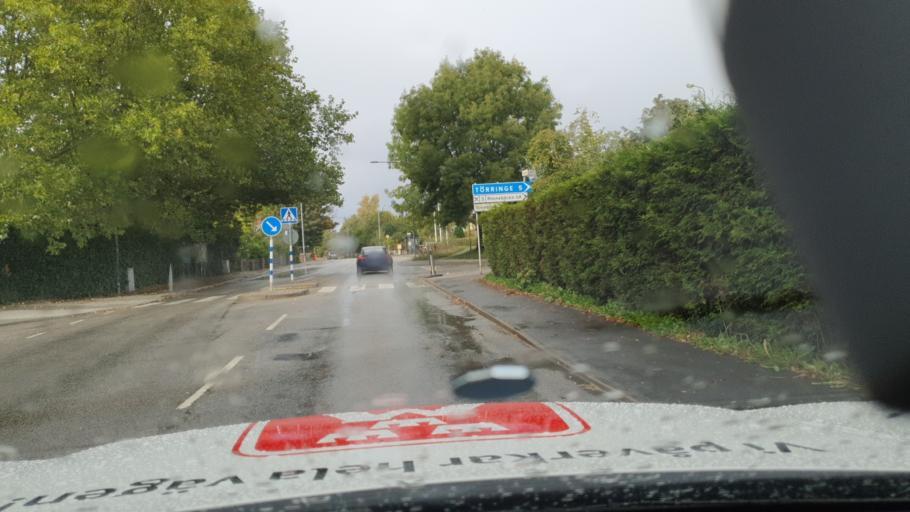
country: SE
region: Skane
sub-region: Malmo
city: Oxie
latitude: 55.5305
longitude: 13.0768
